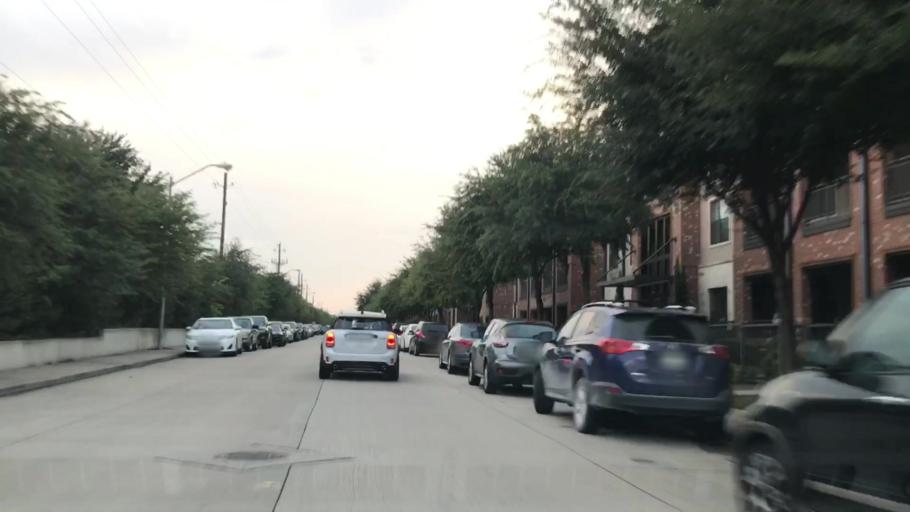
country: US
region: Texas
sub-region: Dallas County
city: Addison
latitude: 33.0110
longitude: -96.8226
